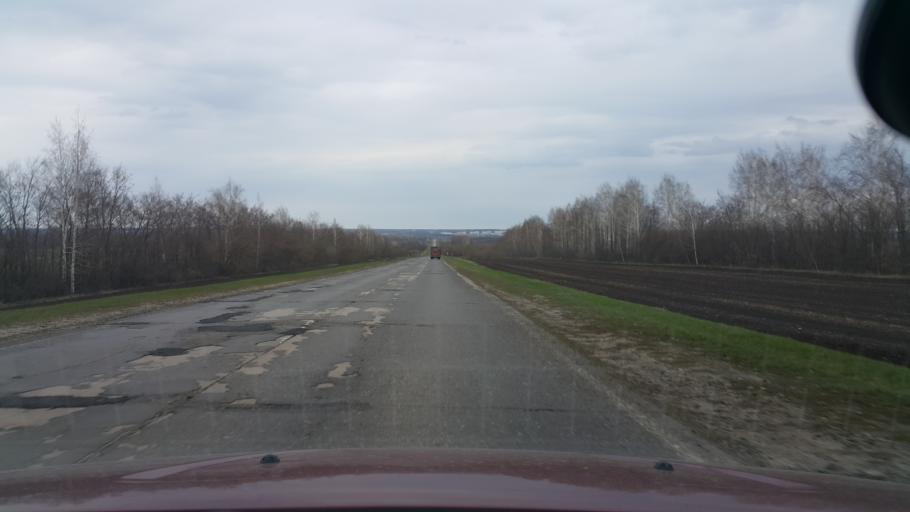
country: RU
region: Tambov
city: Bokino
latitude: 52.5726
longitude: 41.4161
